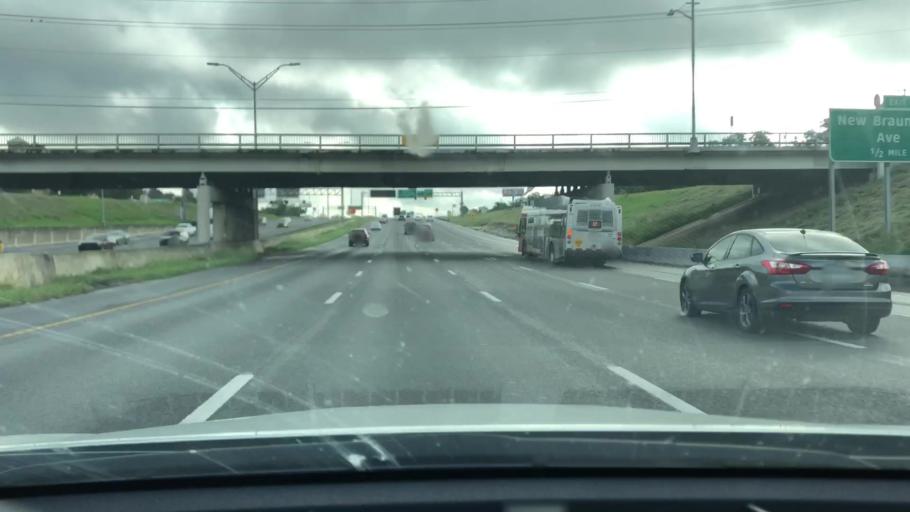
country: US
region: Texas
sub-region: Bexar County
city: San Antonio
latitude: 29.4381
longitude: -98.4707
